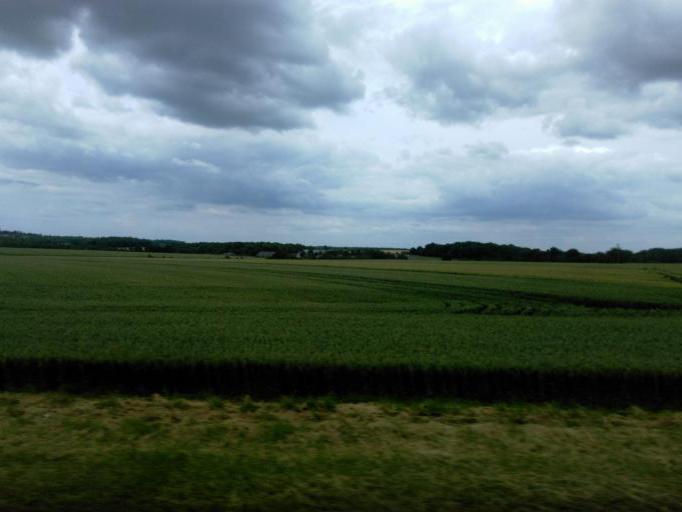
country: FR
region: Ile-de-France
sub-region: Departement du Val-d'Oise
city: Osny
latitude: 49.0967
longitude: 2.0490
